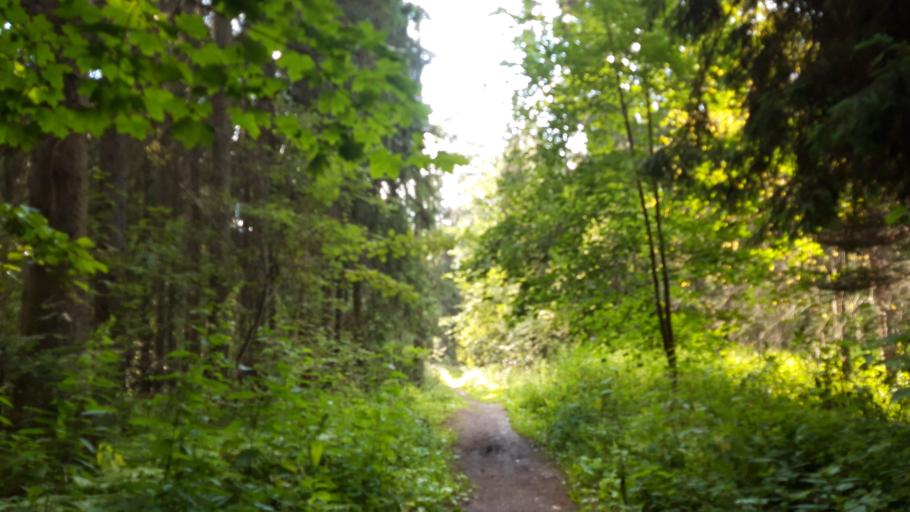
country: RU
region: Tverskaya
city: Konakovo
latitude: 56.6907
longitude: 36.7068
